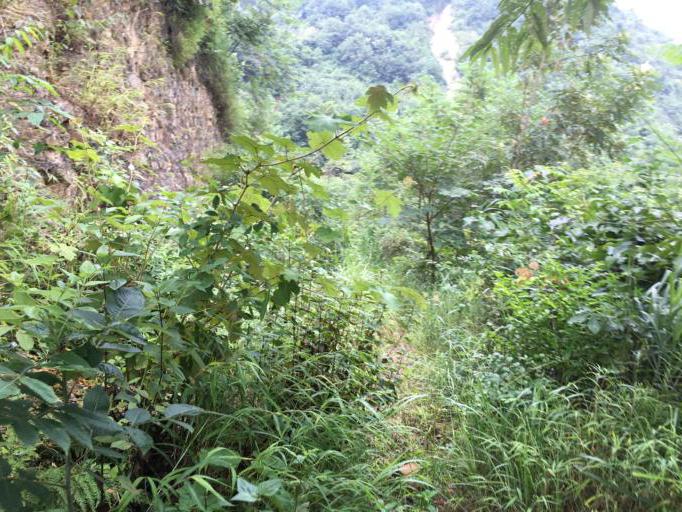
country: CN
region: Guangxi Zhuangzu Zizhiqu
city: Tongle
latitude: 25.3010
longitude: 106.1473
